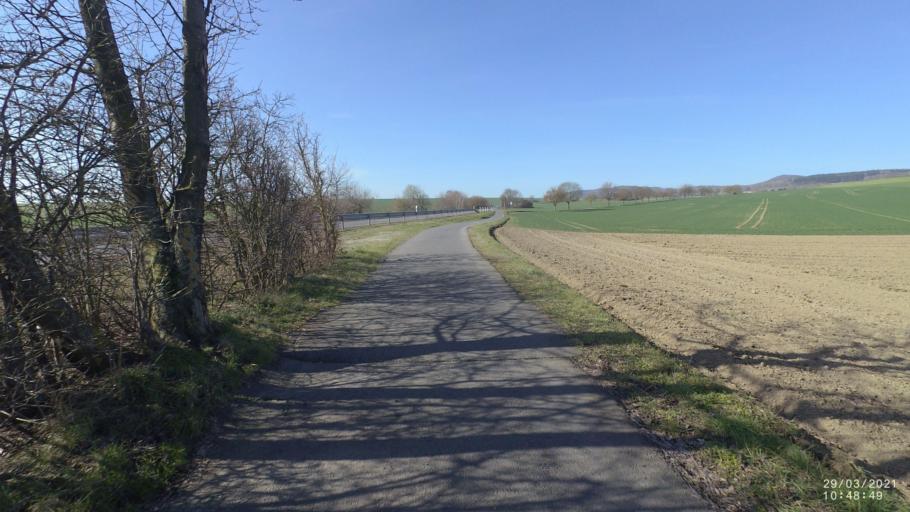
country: DE
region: Rheinland-Pfalz
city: Kretz
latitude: 50.4249
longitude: 7.3721
